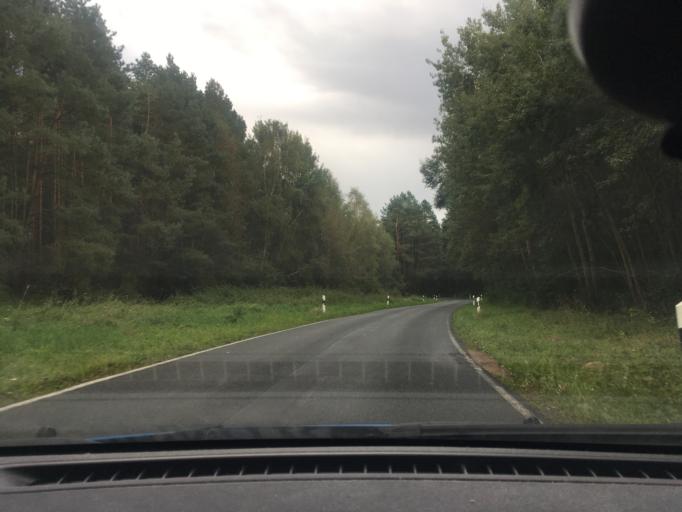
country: DE
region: Mecklenburg-Vorpommern
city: Boizenburg
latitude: 53.3529
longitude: 10.8411
